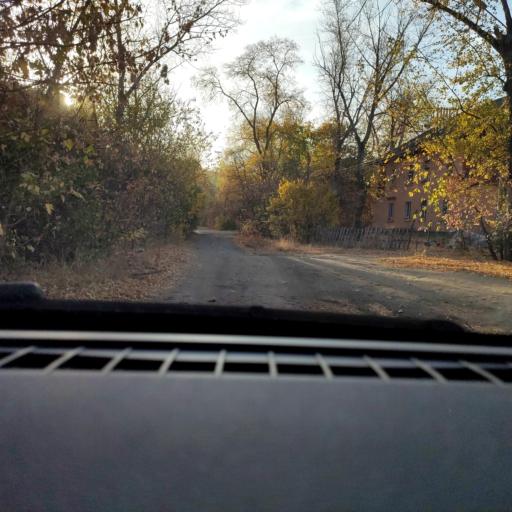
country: RU
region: Voronezj
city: Voronezh
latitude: 51.6650
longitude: 39.2755
